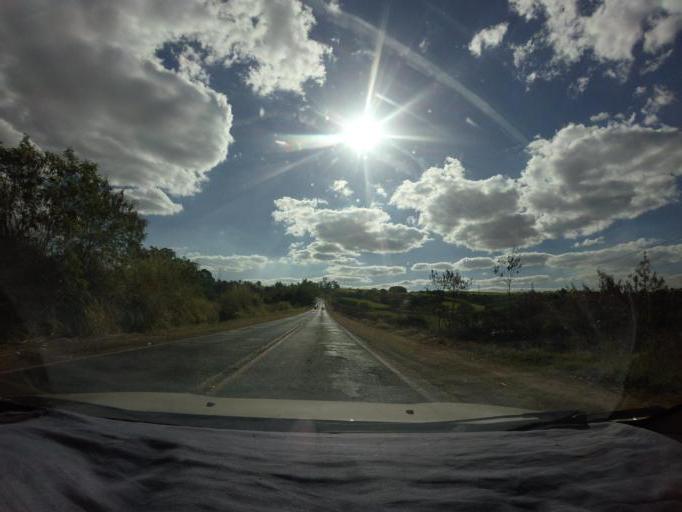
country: BR
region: Sao Paulo
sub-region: Piracicaba
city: Piracicaba
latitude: -22.7355
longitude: -47.5424
